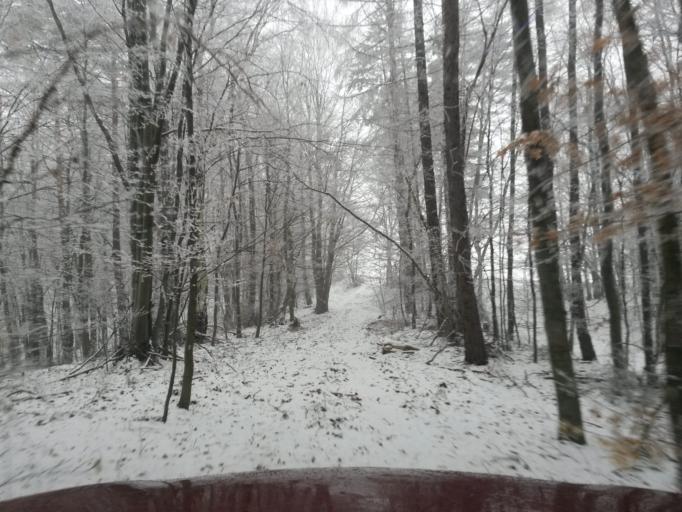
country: SK
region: Presovsky
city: Sabinov
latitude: 48.9778
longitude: 21.0915
